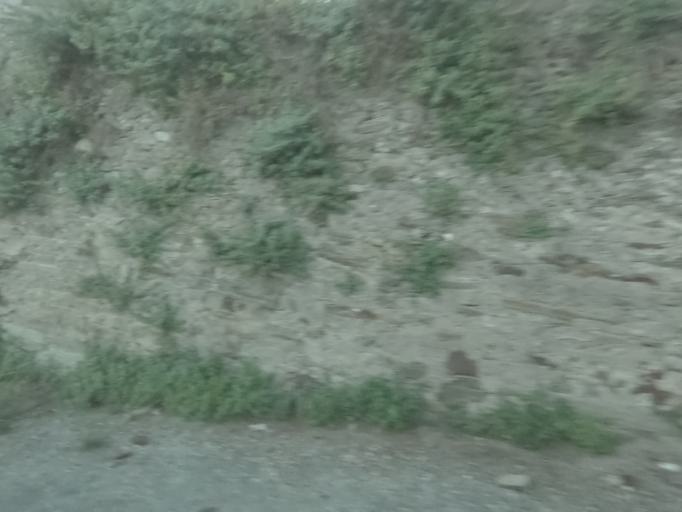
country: PT
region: Vila Real
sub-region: Peso da Regua
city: Peso da Regua
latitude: 41.1679
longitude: -7.7588
